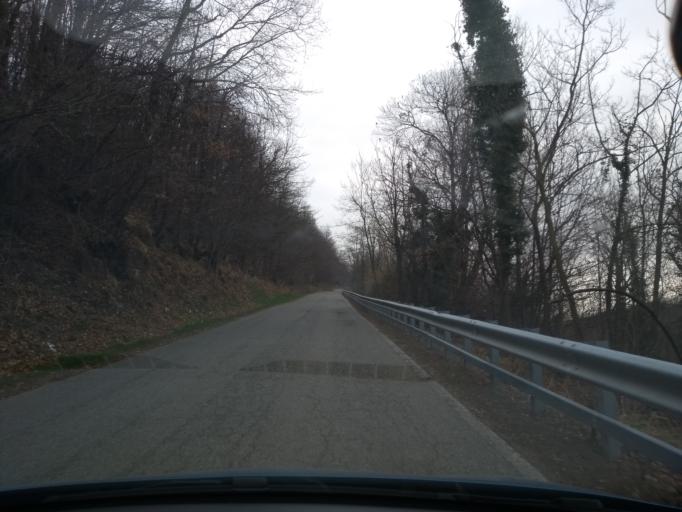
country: IT
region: Piedmont
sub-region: Provincia di Torino
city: Palazzo Canavese
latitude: 45.4725
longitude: 7.9755
